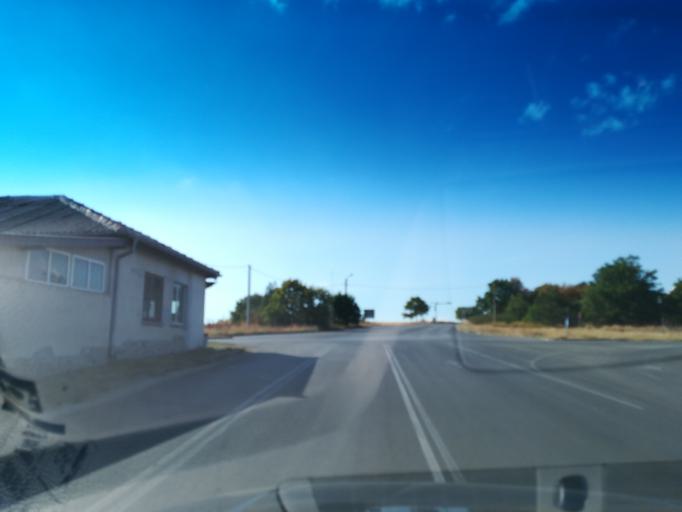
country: BG
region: Khaskovo
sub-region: Obshtina Mineralni Bani
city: Mineralni Bani
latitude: 42.0209
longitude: 25.4134
